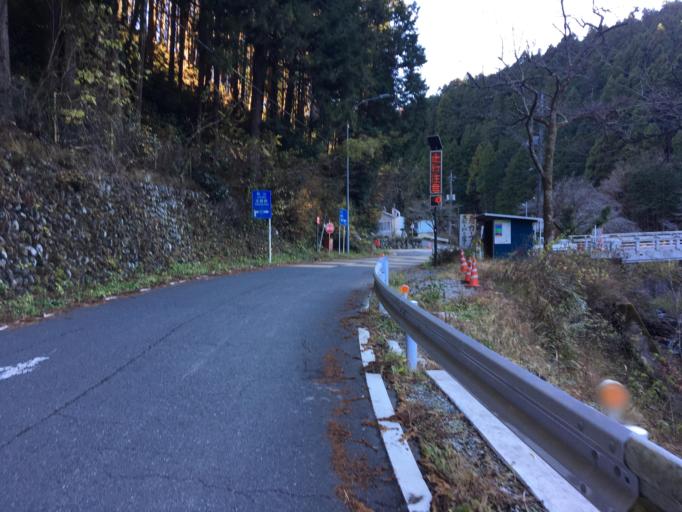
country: JP
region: Saitama
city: Ogawa
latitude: 36.0172
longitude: 139.1736
